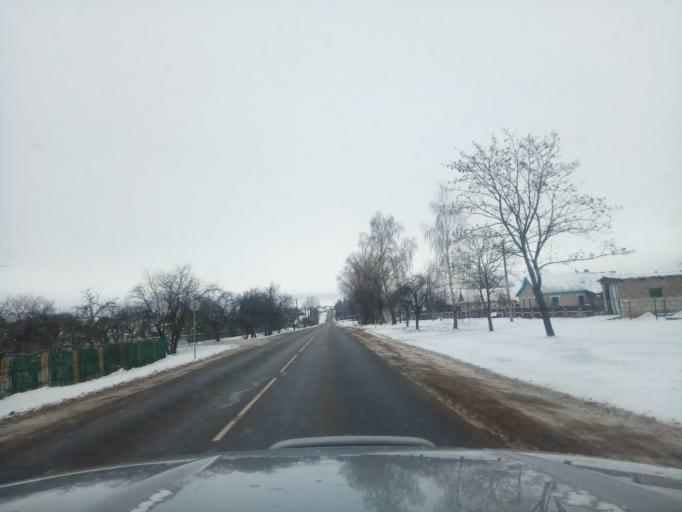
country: BY
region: Minsk
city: Kapyl'
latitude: 53.1583
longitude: 27.0973
